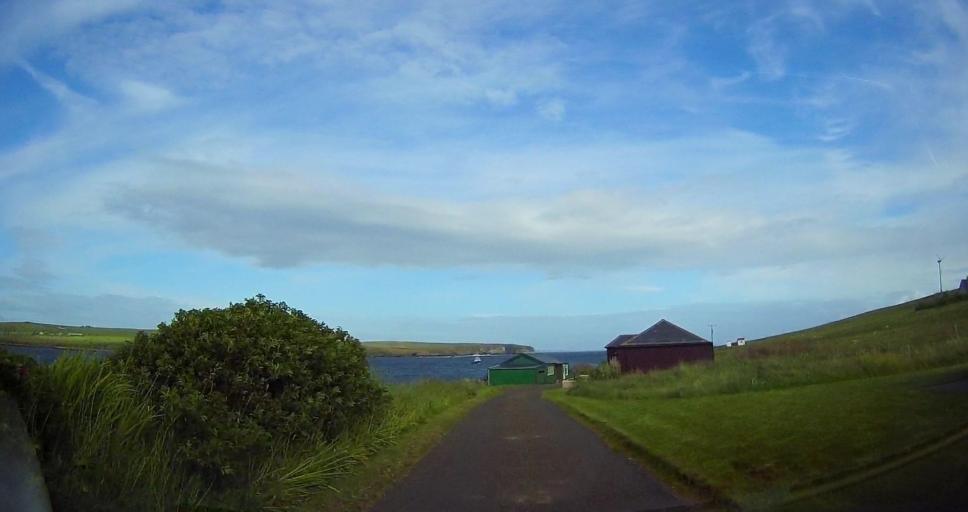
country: GB
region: Scotland
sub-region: Orkney Islands
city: Stromness
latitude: 58.7807
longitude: -3.2326
